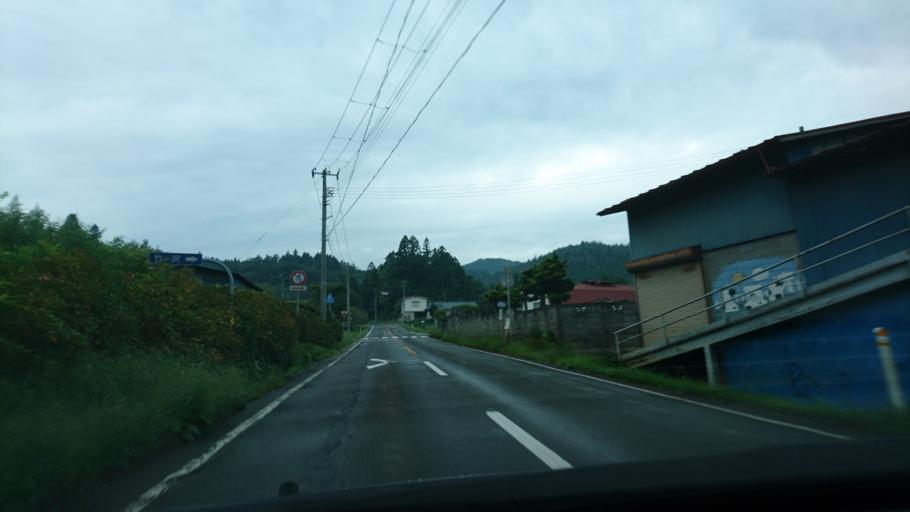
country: JP
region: Iwate
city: Ichinoseki
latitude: 39.0174
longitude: 141.2344
